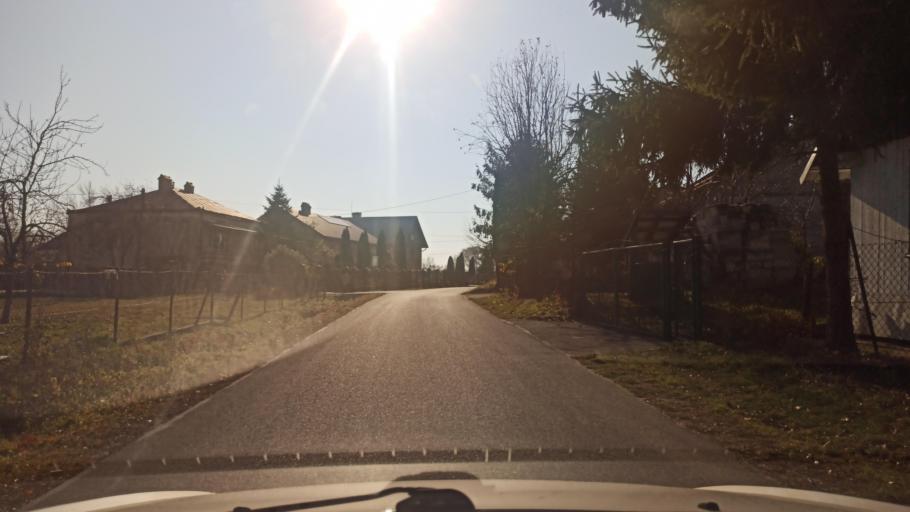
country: PL
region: Subcarpathian Voivodeship
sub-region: Powiat jaroslawski
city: Radymno
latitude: 49.9419
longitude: 22.8155
